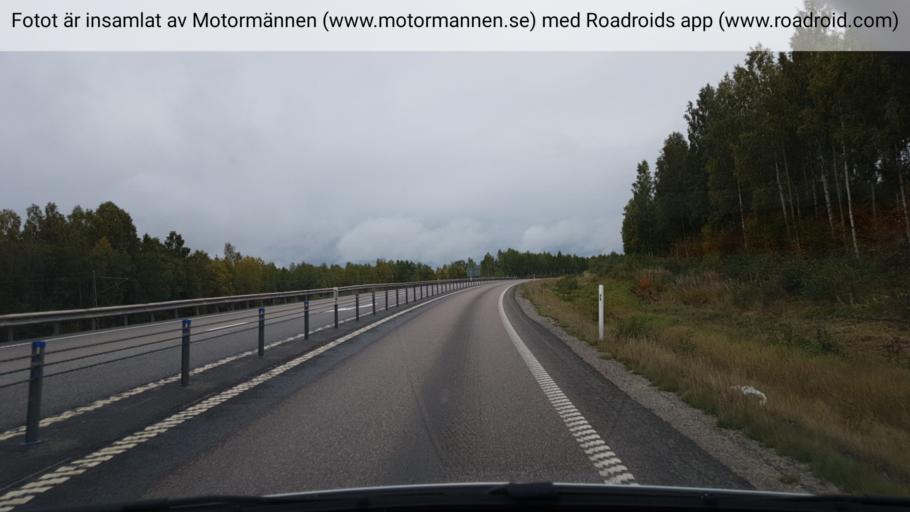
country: SE
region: Vaesternorrland
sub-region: Sundsvalls Kommun
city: Njurundabommen
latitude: 62.1630
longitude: 17.3554
